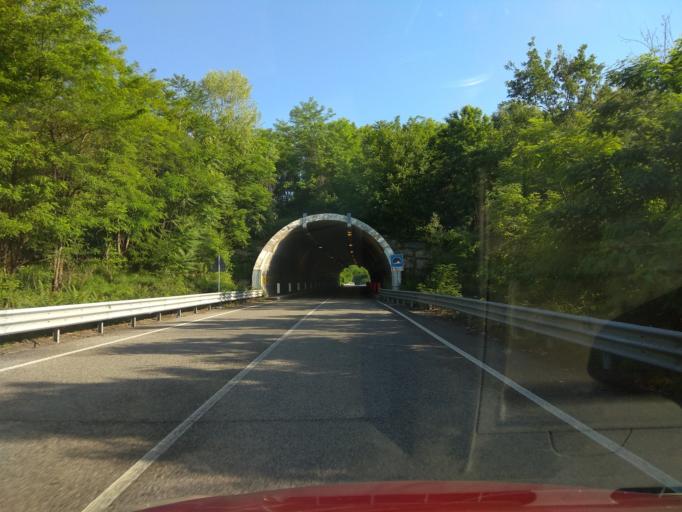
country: IT
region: Piedmont
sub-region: Provincia di Biella
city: Quaregna
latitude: 45.5953
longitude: 8.1698
